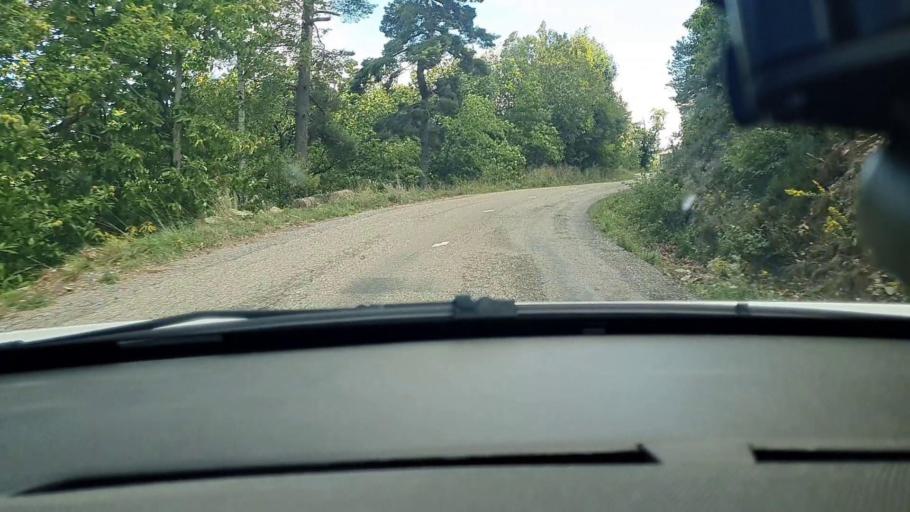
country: FR
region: Rhone-Alpes
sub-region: Departement de l'Ardeche
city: Les Vans
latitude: 44.4144
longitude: 4.0189
